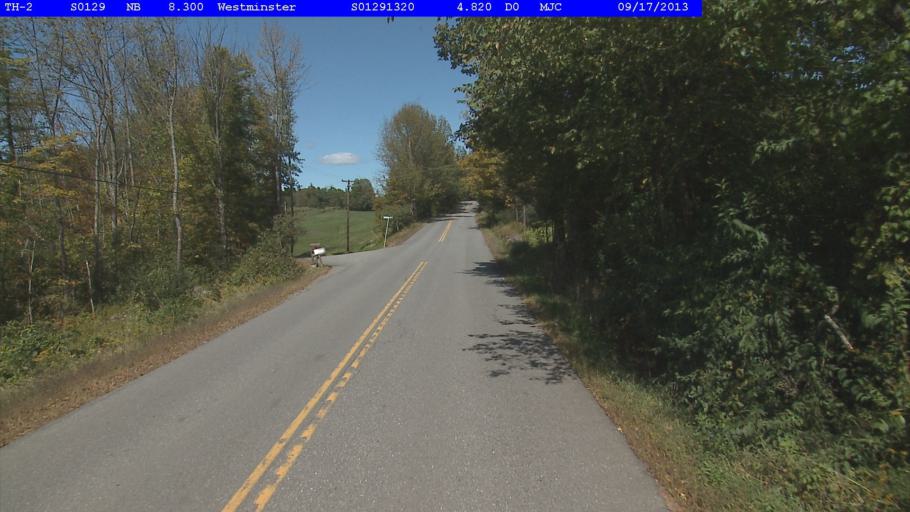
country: US
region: Vermont
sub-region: Windham County
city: Bellows Falls
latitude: 43.0844
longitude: -72.5358
